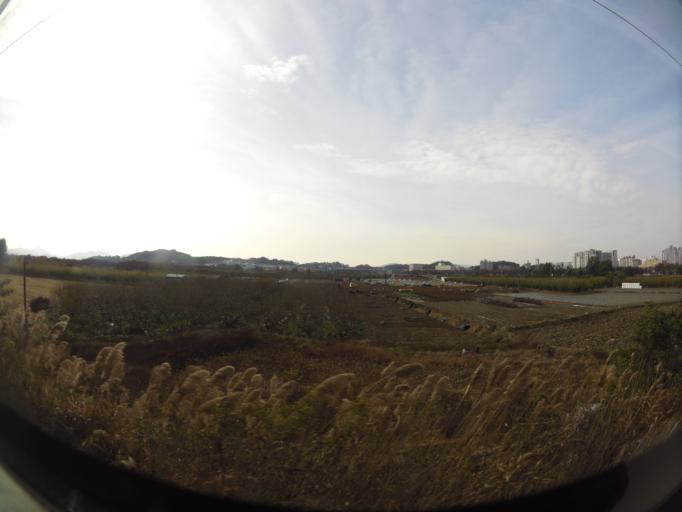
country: KR
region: Daejeon
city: Songgang-dong
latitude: 36.5881
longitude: 127.3060
